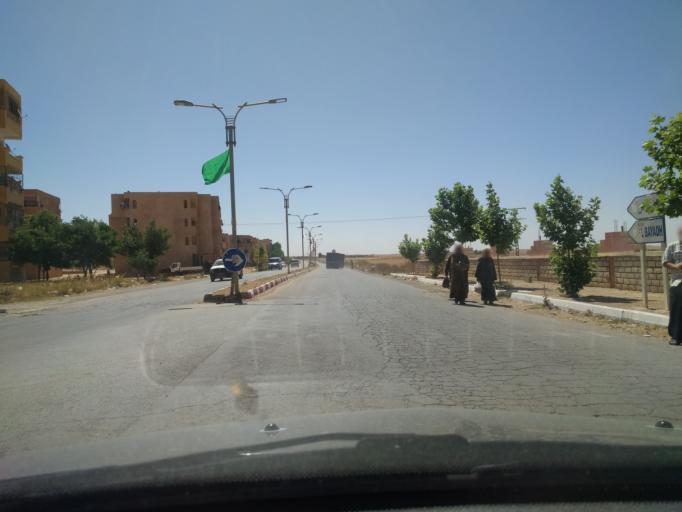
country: DZ
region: Tiaret
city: Frenda
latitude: 34.9041
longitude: 1.1120
